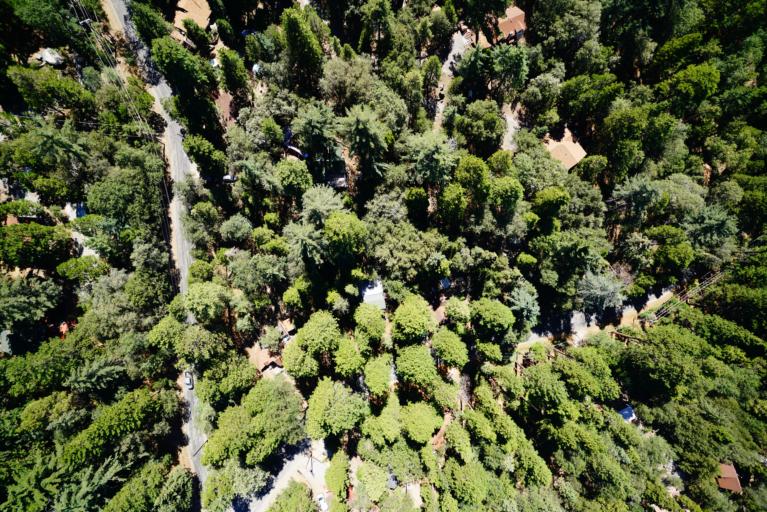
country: US
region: California
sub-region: Riverside County
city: Idyllwild-Pine Cove
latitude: 33.7561
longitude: -116.7452
